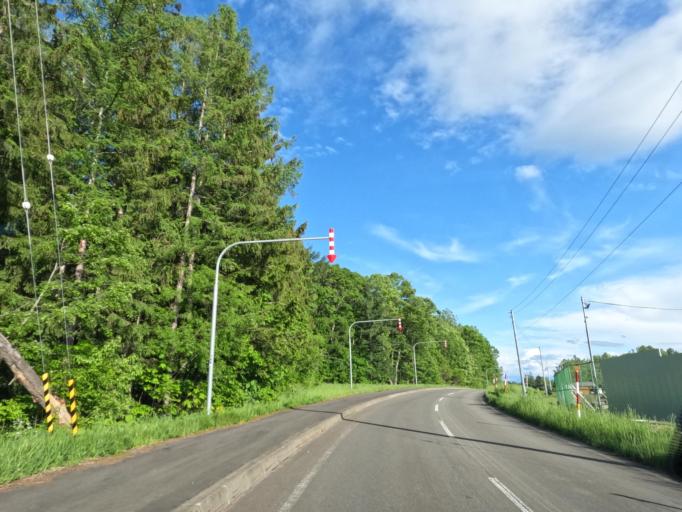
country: JP
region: Hokkaido
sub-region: Asahikawa-shi
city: Asahikawa
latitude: 43.9220
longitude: 142.4985
